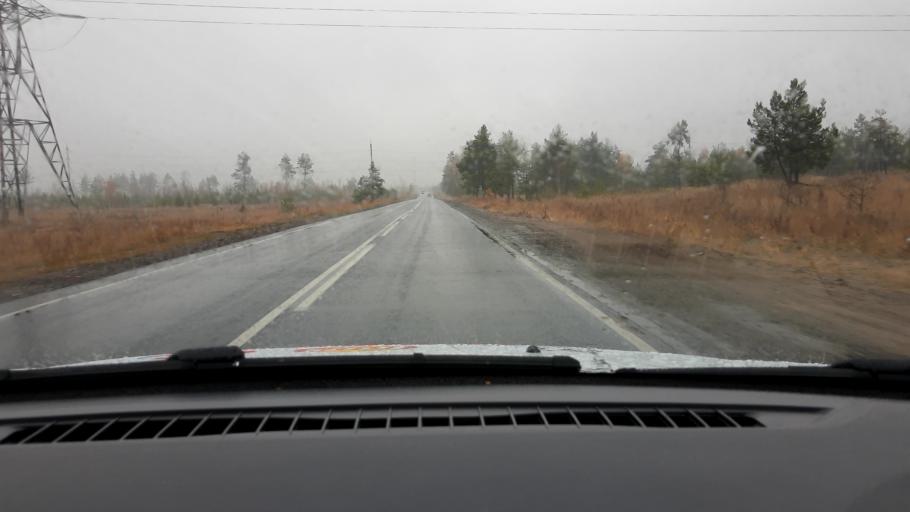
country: RU
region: Nizjnij Novgorod
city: Babino
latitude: 56.2797
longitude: 43.5988
